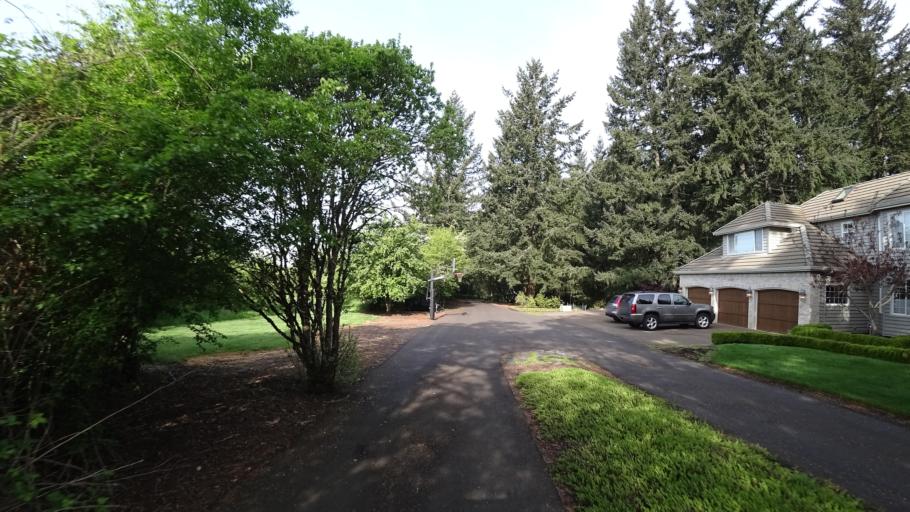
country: US
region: Oregon
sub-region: Washington County
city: Aloha
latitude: 45.4414
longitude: -122.8592
